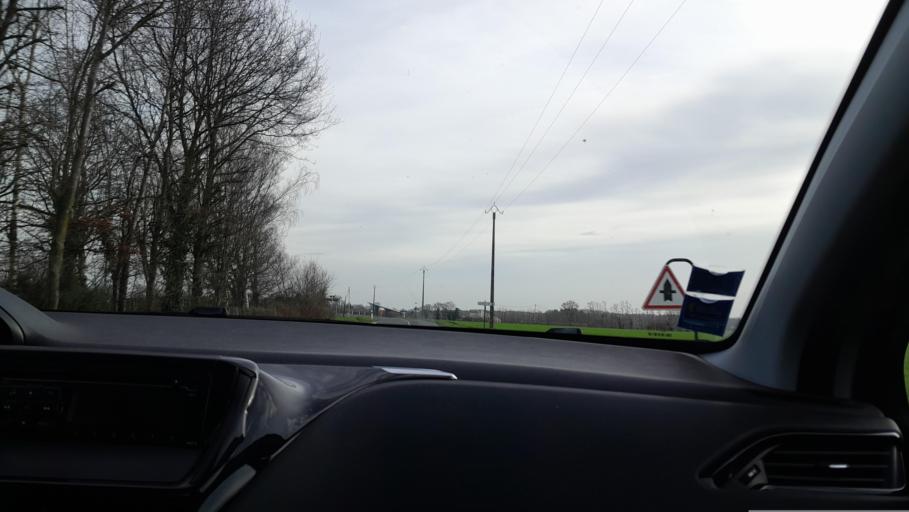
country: FR
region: Brittany
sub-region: Departement d'Ille-et-Vilaine
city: La Guerche-de-Bretagne
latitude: 47.9510
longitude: -1.1899
